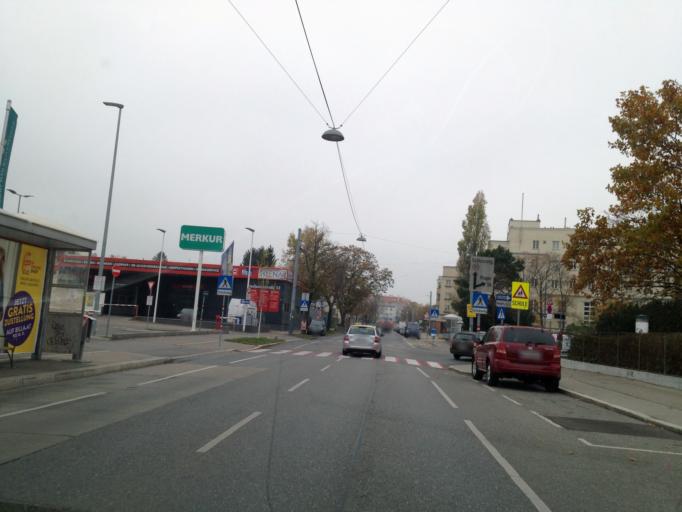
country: AT
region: Vienna
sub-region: Wien Stadt
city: Vienna
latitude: 48.2596
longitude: 16.3893
